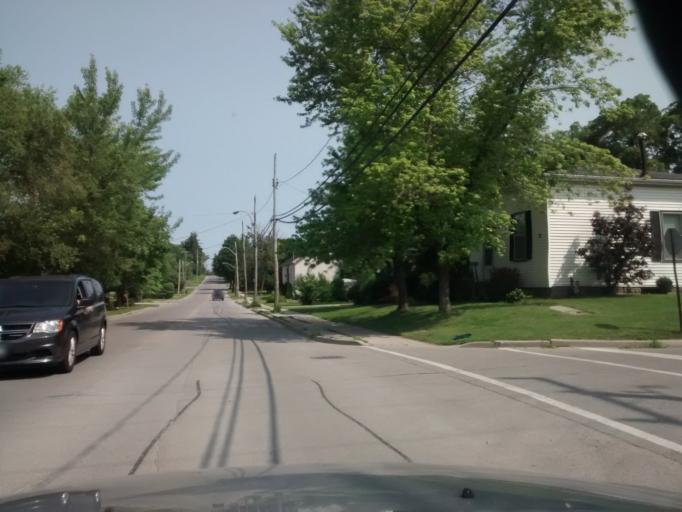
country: CA
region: Ontario
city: Ancaster
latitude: 42.9520
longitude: -79.8565
